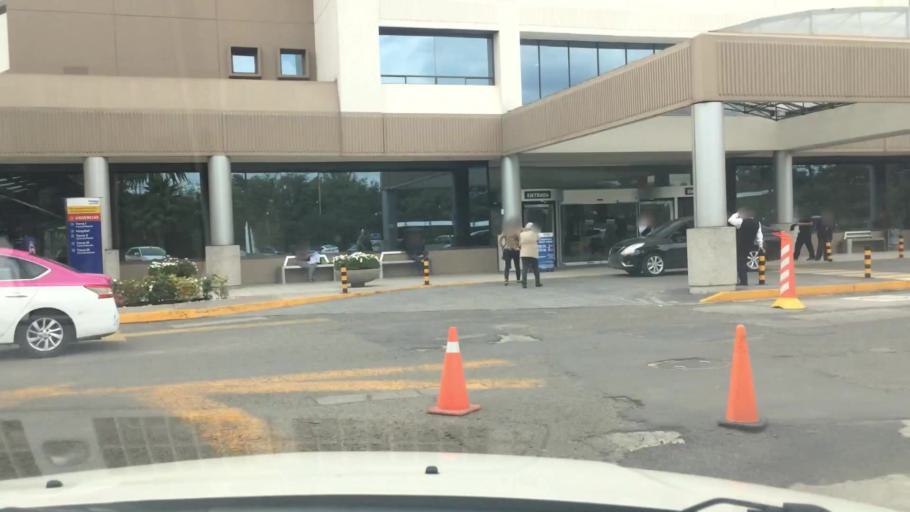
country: MX
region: Mexico City
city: Tlalpan
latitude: 19.2968
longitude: -99.1610
